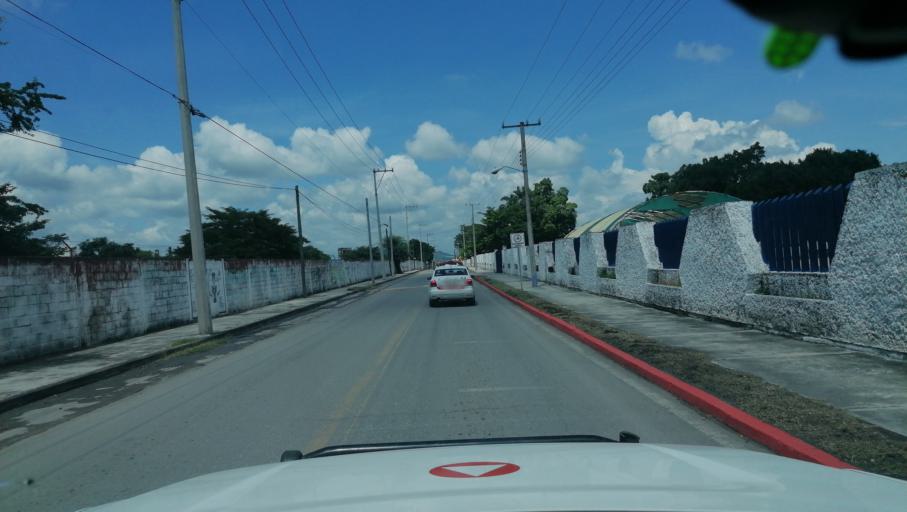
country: MX
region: Morelos
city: Zacatepec
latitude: 18.6501
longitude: -99.1843
